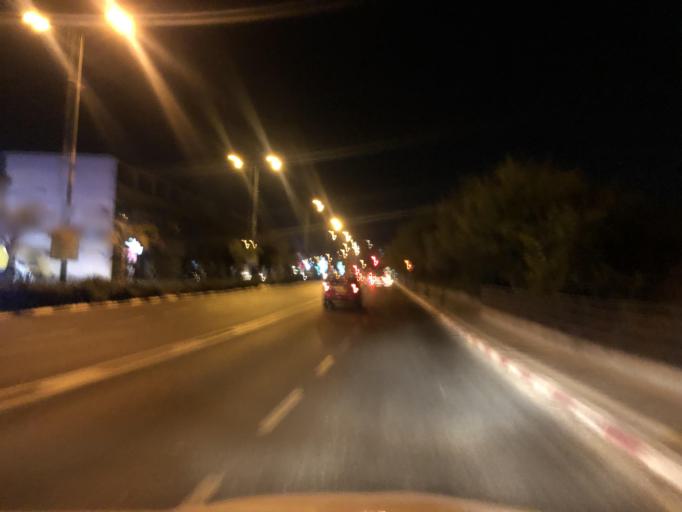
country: IL
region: Tel Aviv
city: Yafo
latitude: 32.0506
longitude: 34.7713
